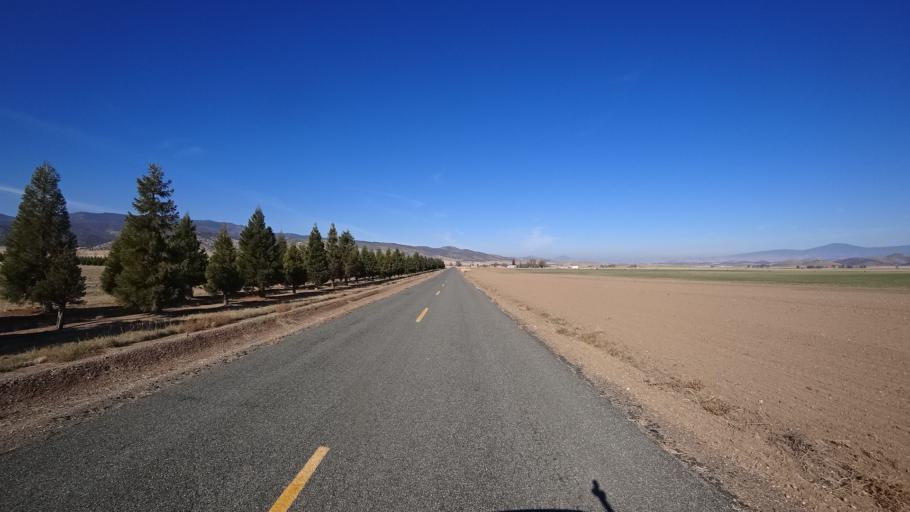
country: US
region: California
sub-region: Siskiyou County
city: Montague
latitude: 41.5523
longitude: -122.5448
